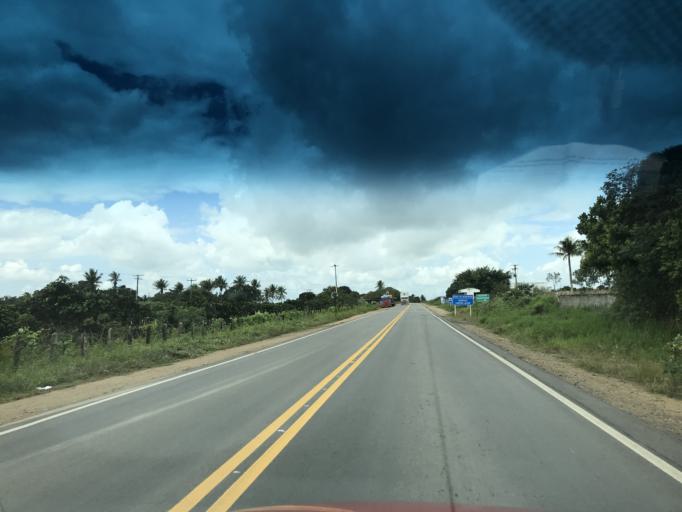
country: BR
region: Bahia
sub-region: Conceicao Do Almeida
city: Conceicao do Almeida
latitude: -12.6927
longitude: -39.2456
